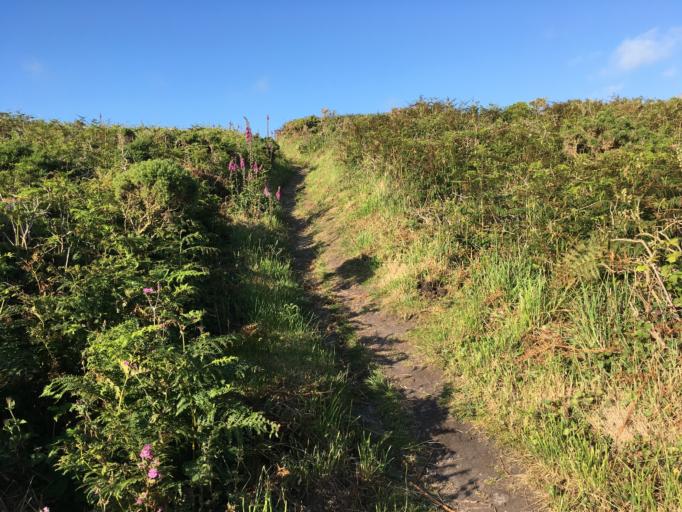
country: GB
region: England
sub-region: Cornwall
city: Saint Just
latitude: 50.1200
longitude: -5.6972
